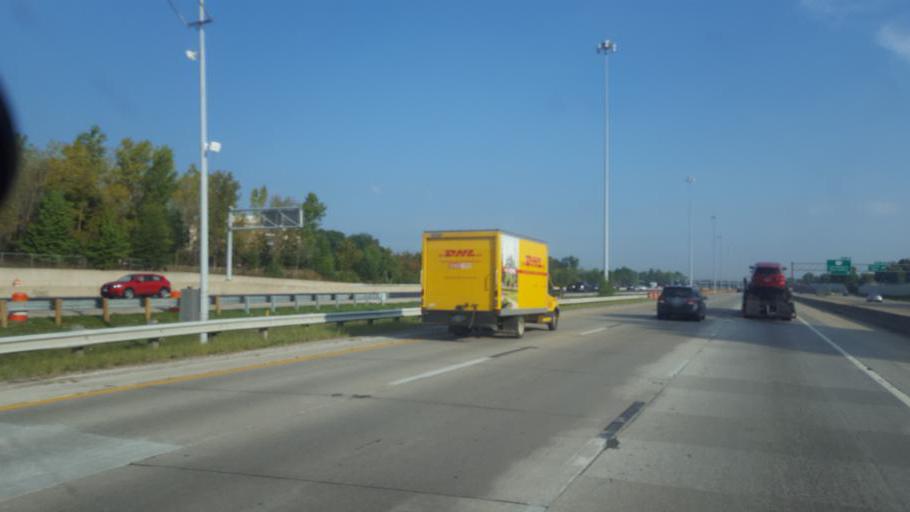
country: US
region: Ohio
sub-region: Franklin County
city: Gahanna
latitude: 40.0408
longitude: -82.9025
